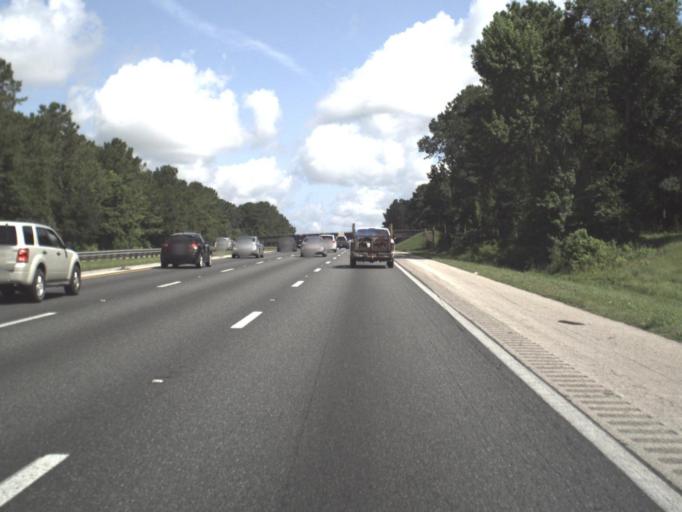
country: US
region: Florida
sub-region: Alachua County
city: Gainesville
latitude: 29.5200
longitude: -82.3077
